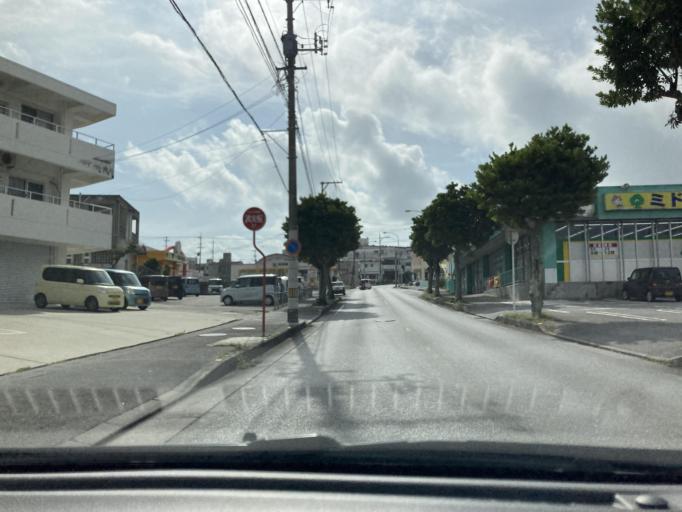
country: JP
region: Okinawa
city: Ginowan
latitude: 26.2619
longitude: 127.7626
